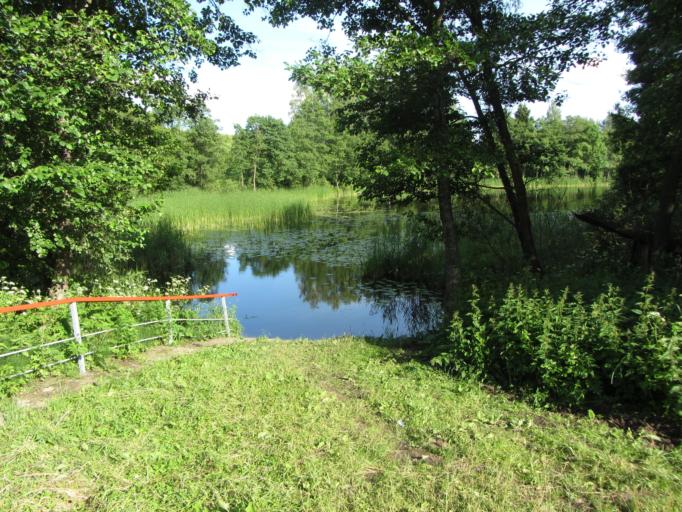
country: BY
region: Vitebsk
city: Lyntupy
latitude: 55.2270
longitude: 26.3359
